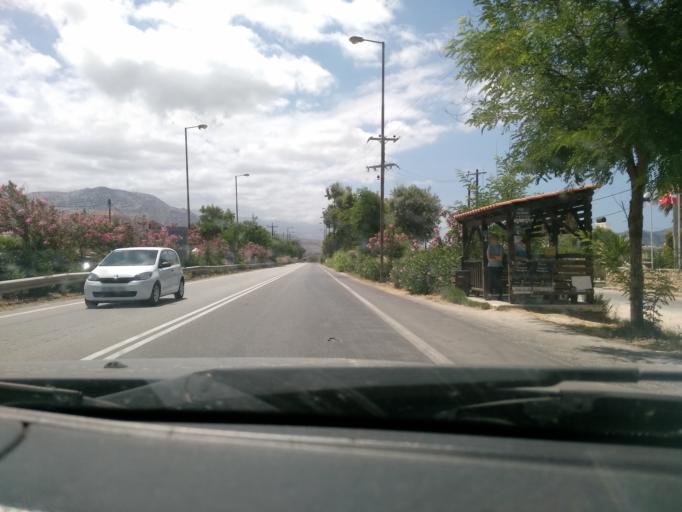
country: GR
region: Crete
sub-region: Nomos Chanias
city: Georgioupolis
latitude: 35.3511
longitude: 24.3009
